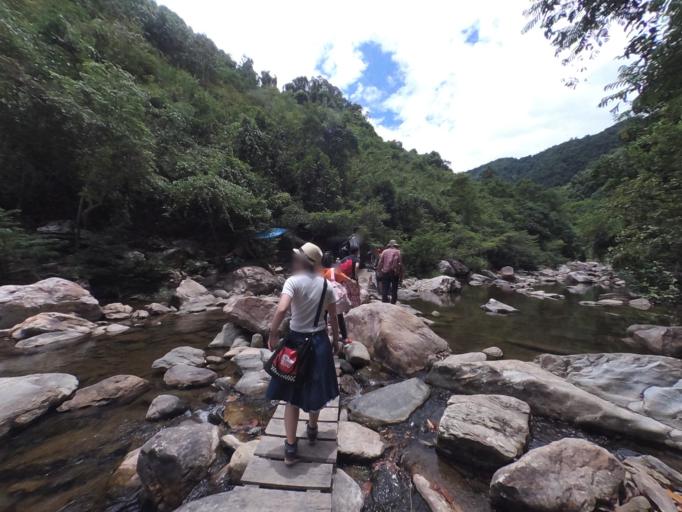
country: VN
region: Thua Thien-Hue
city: A Luoi
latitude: 16.3050
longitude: 107.3246
